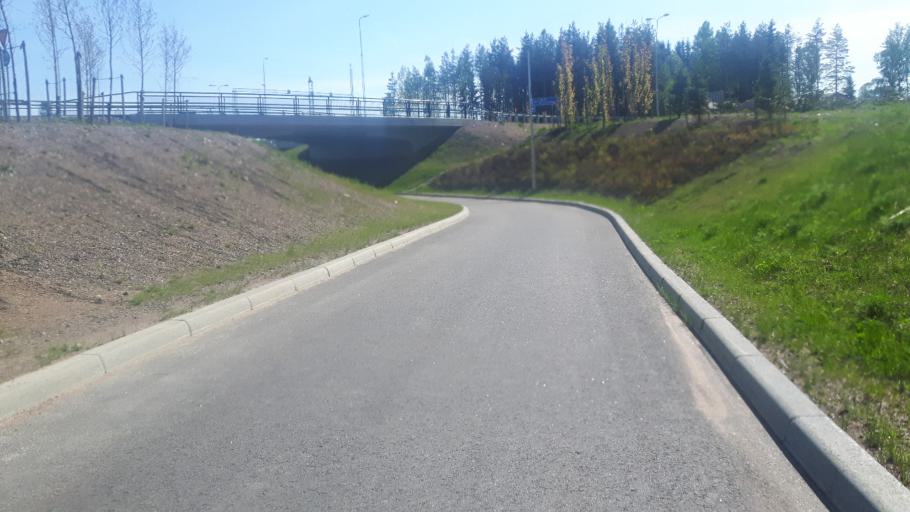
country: FI
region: Kymenlaakso
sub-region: Kotka-Hamina
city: Virojoki
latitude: 60.6000
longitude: 27.8259
